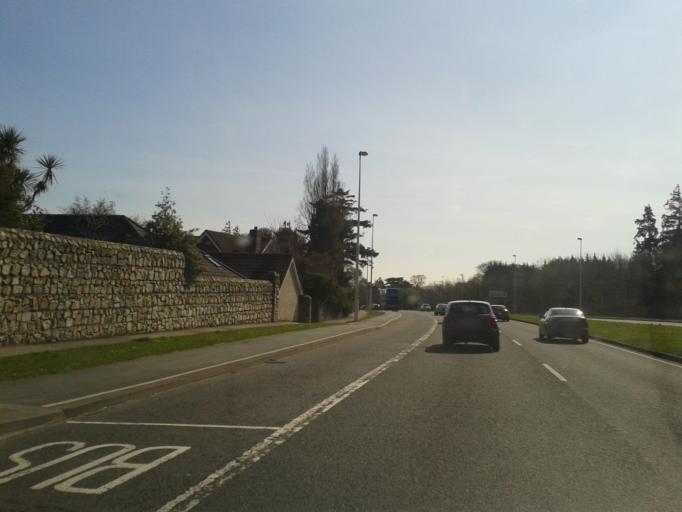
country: IE
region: Leinster
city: Foxrock
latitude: 53.2755
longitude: -6.1791
